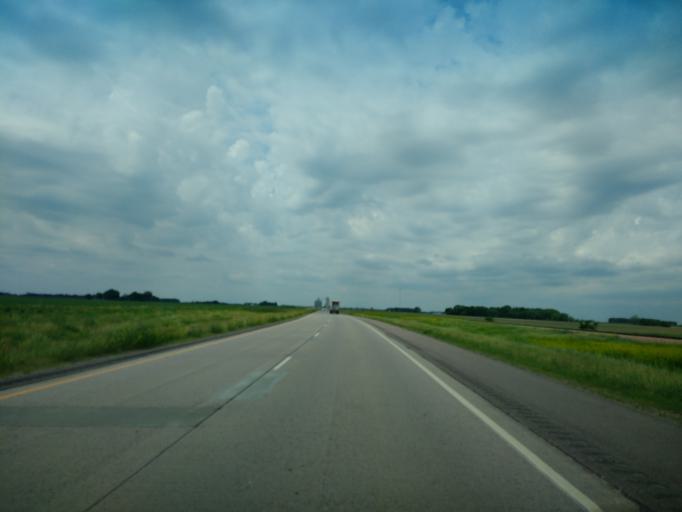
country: US
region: Minnesota
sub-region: Cottonwood County
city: Mountain Lake
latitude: 43.9495
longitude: -94.8468
